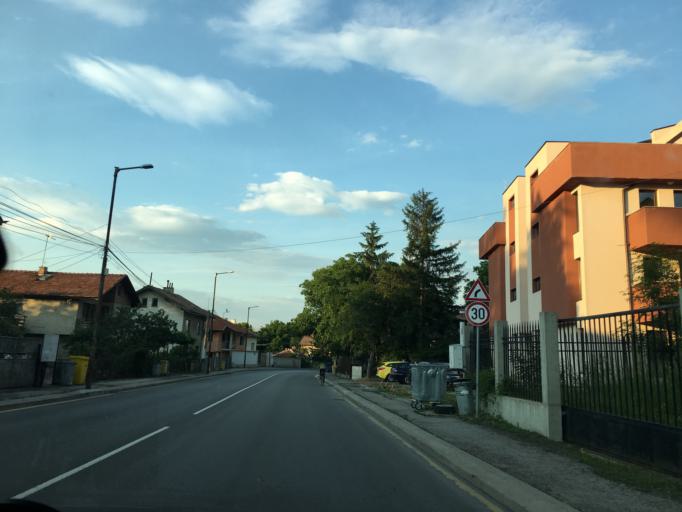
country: BG
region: Sofiya
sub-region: Obshtina Bozhurishte
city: Bozhurishte
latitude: 42.7133
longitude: 23.1671
